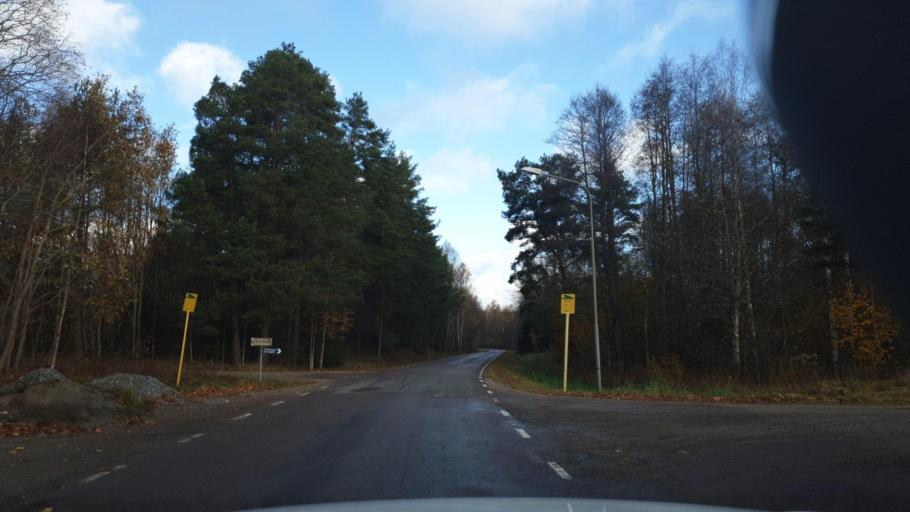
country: SE
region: Vaermland
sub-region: Grums Kommun
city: Slottsbron
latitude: 59.4754
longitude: 12.8836
